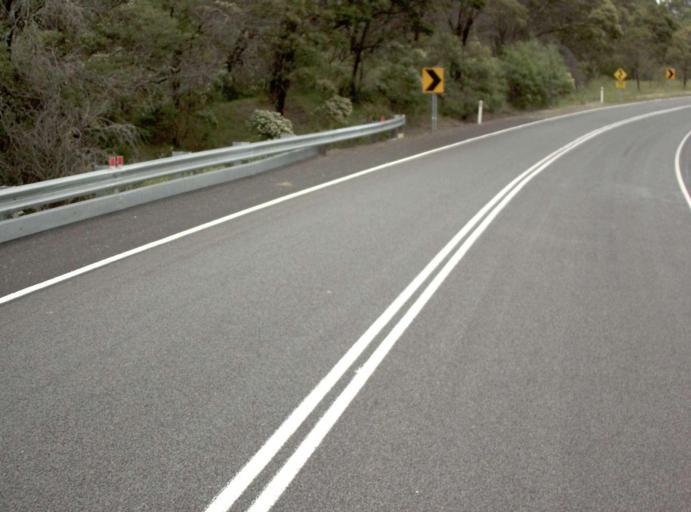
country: AU
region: New South Wales
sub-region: Bombala
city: Bombala
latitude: -37.2398
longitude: 149.2633
